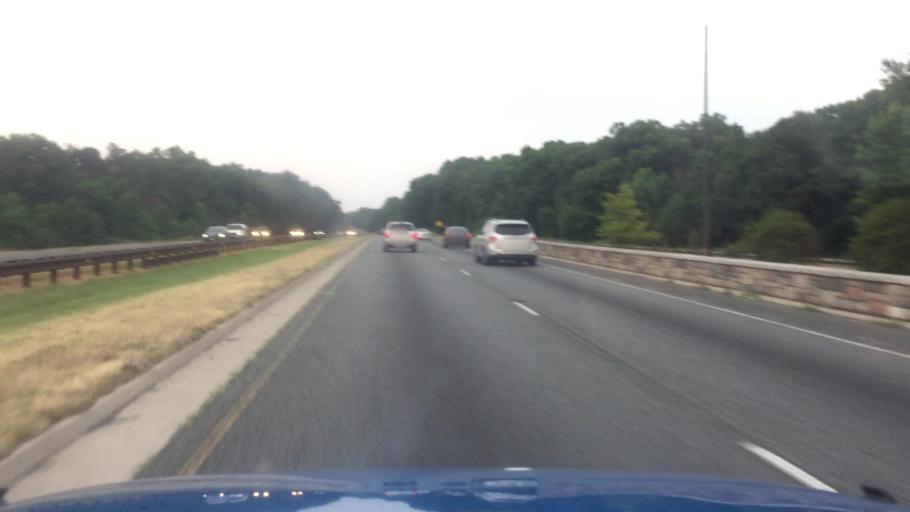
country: US
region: Maryland
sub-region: Prince George's County
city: Greenbelt
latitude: 39.0330
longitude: -76.8524
